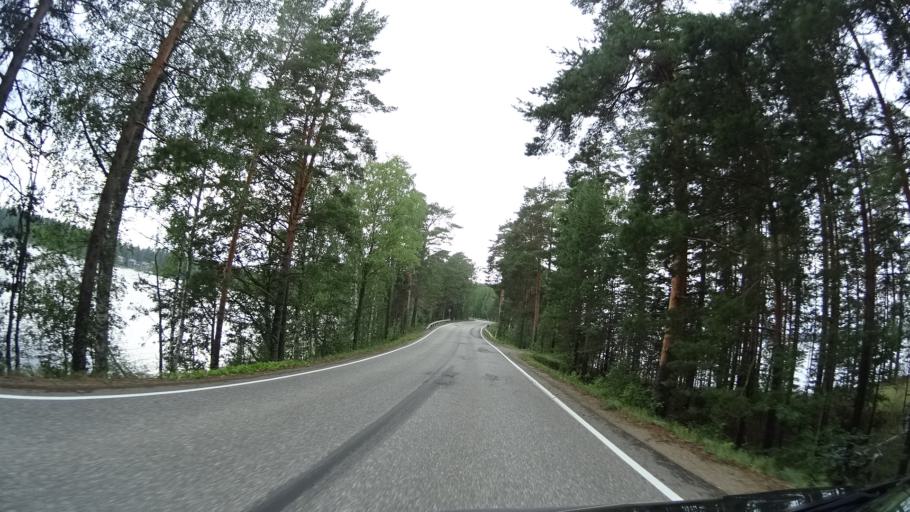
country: FI
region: Southern Savonia
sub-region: Savonlinna
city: Punkaharju
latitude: 61.7568
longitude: 29.4088
